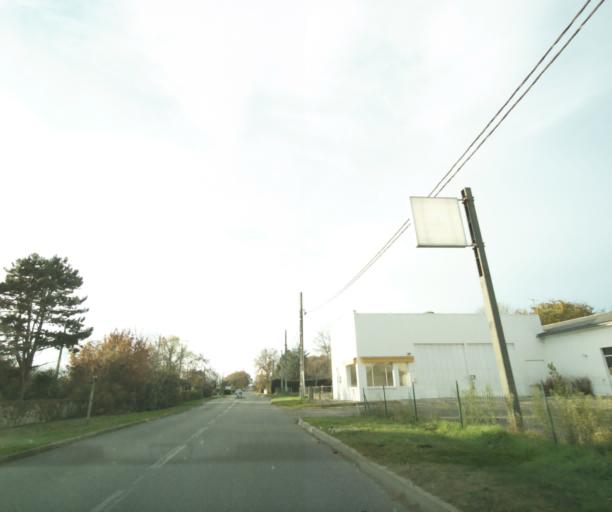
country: FR
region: Aquitaine
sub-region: Departement des Landes
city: Gabarret
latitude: 43.9875
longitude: 0.0035
